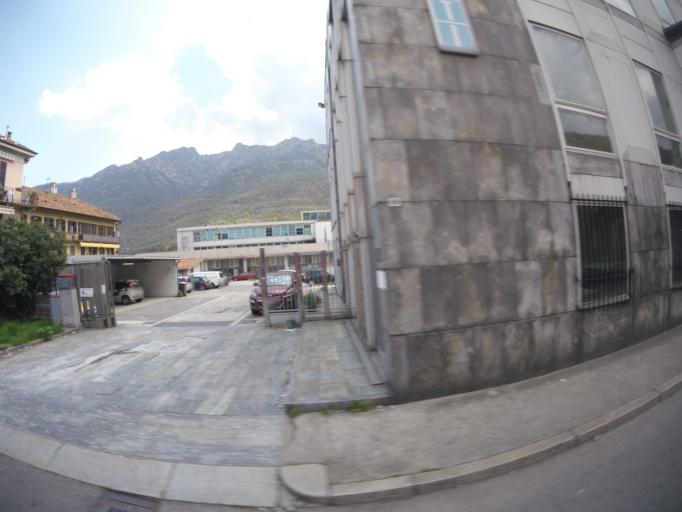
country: IT
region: Piedmont
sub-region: Provincia Verbano-Cusio-Ossola
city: Omegna
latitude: 45.8900
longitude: 8.4098
